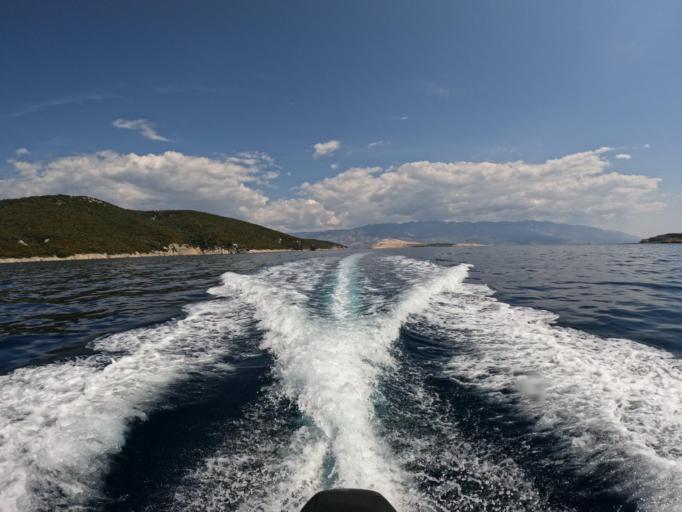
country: HR
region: Primorsko-Goranska
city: Lopar
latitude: 44.8553
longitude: 14.7475
